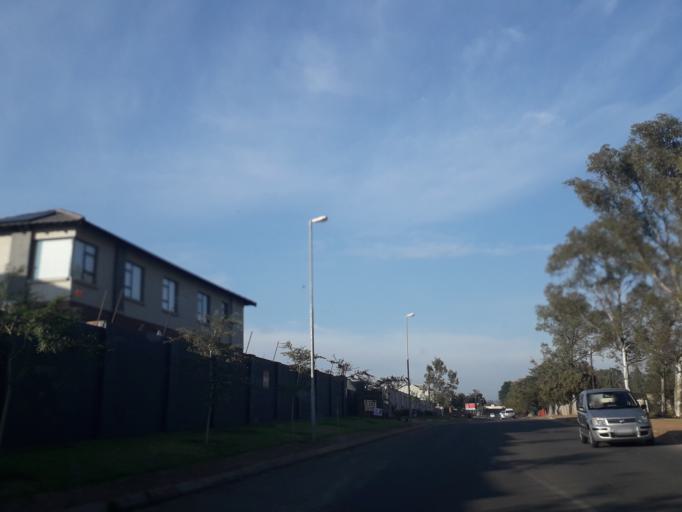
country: ZA
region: Gauteng
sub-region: City of Johannesburg Metropolitan Municipality
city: Roodepoort
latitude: -26.0884
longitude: 27.9046
